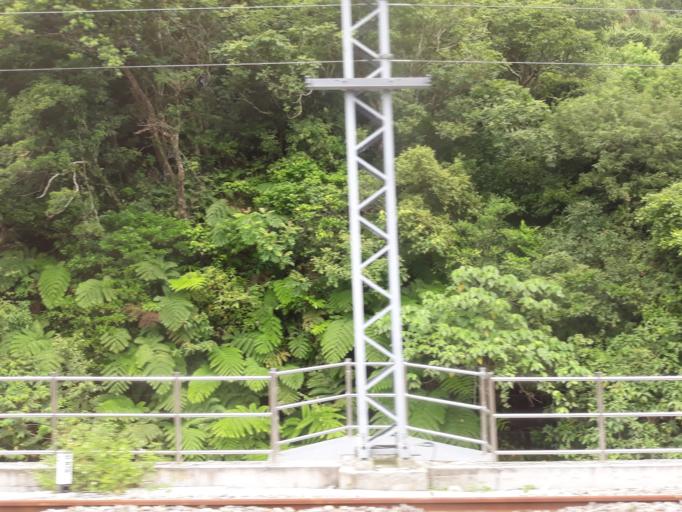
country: TW
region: Taiwan
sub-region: Yilan
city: Yilan
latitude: 24.4466
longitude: 121.7764
